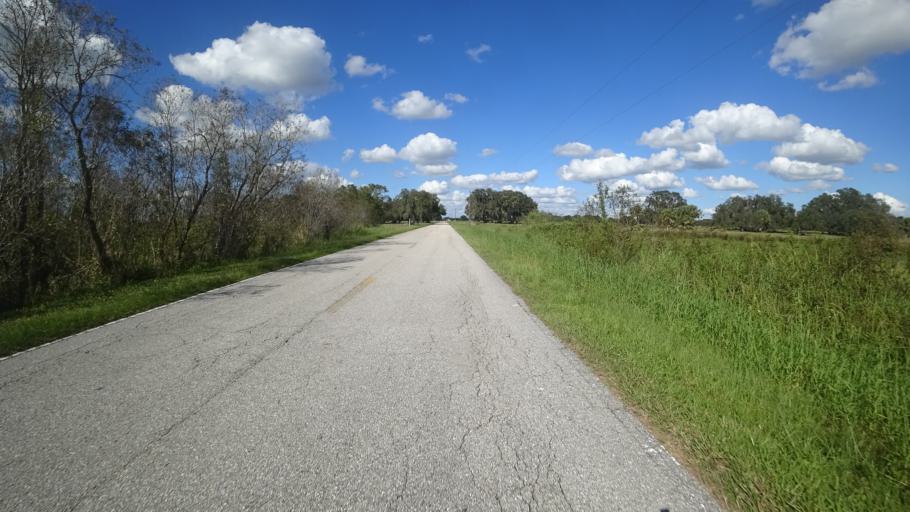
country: US
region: Florida
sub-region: Sarasota County
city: North Port
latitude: 27.1949
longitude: -82.1223
